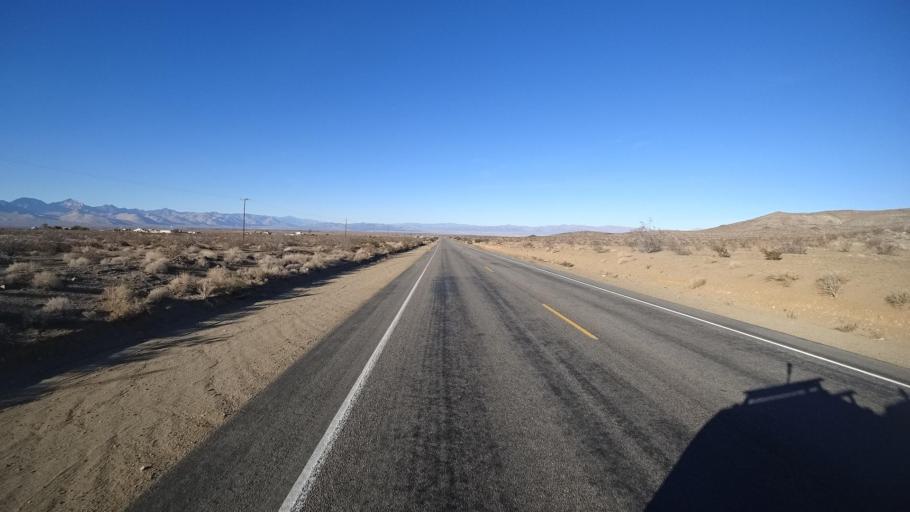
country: US
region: California
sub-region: Kern County
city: Ridgecrest
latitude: 35.5645
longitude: -117.7126
